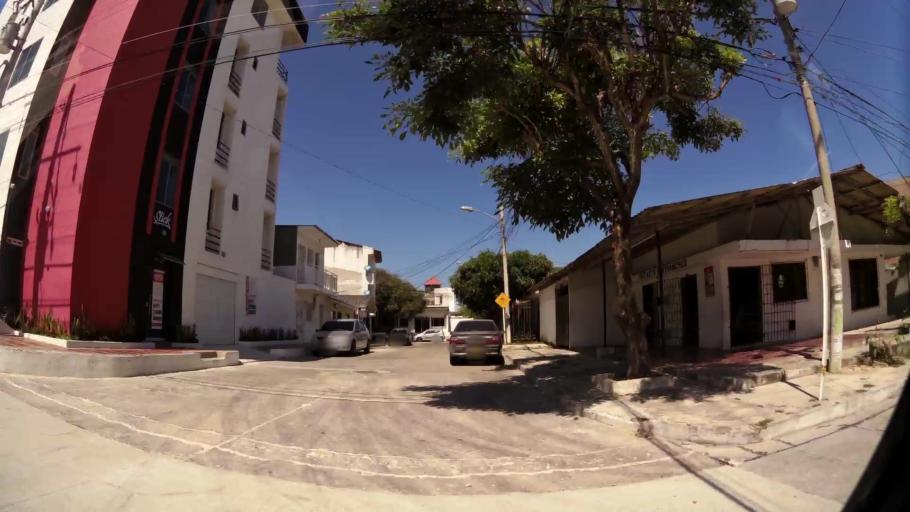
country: CO
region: Atlantico
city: Barranquilla
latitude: 11.0028
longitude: -74.7938
